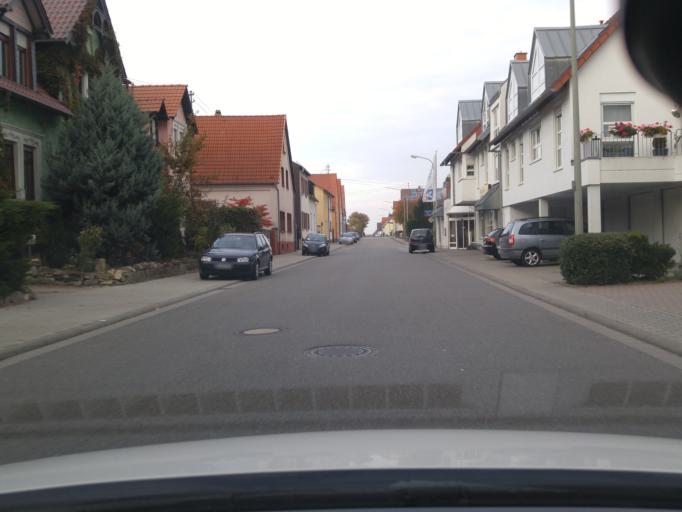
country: DE
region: Rheinland-Pfalz
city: Dudenhofen
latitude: 49.2882
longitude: 8.4000
